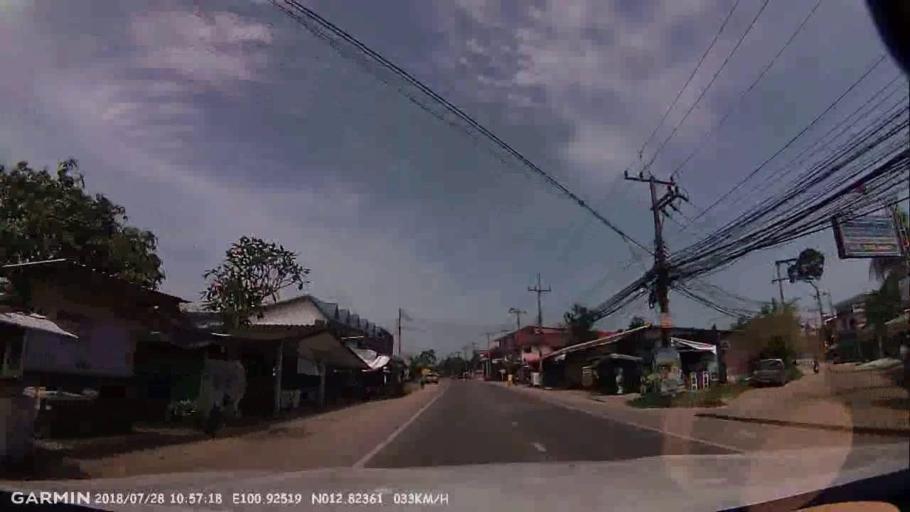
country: TH
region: Chon Buri
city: Phatthaya
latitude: 12.8236
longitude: 100.9251
